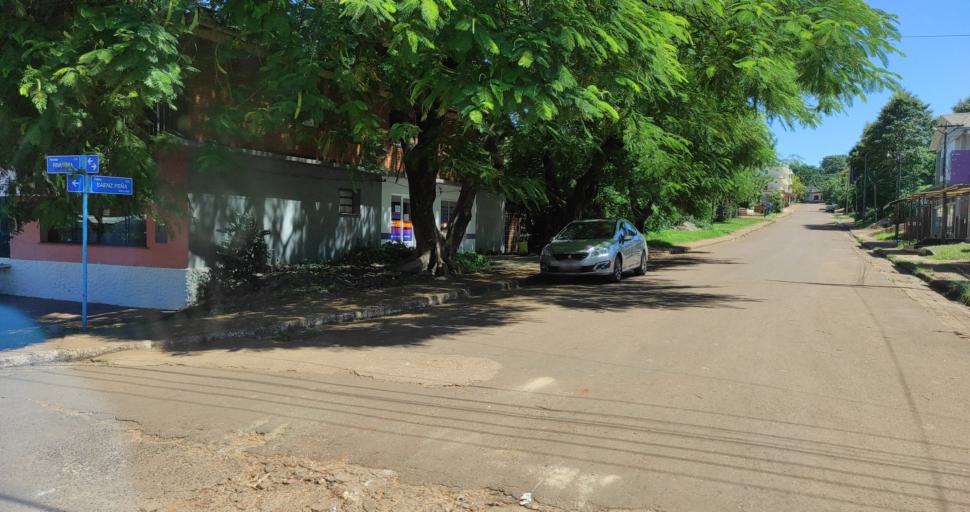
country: AR
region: Misiones
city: El Soberbio
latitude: -27.2962
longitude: -54.1992
